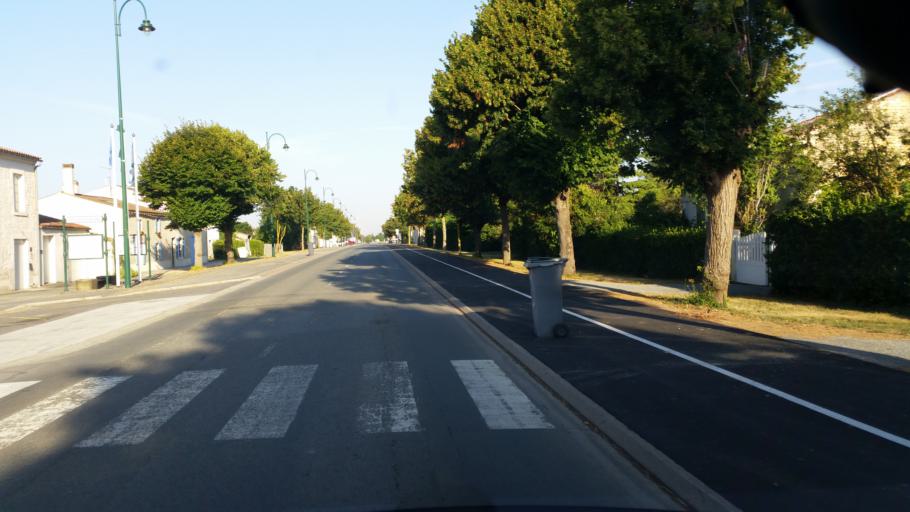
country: FR
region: Poitou-Charentes
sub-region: Departement de la Charente-Maritime
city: Saint-Jean-de-Liversay
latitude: 46.2272
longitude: -0.8640
